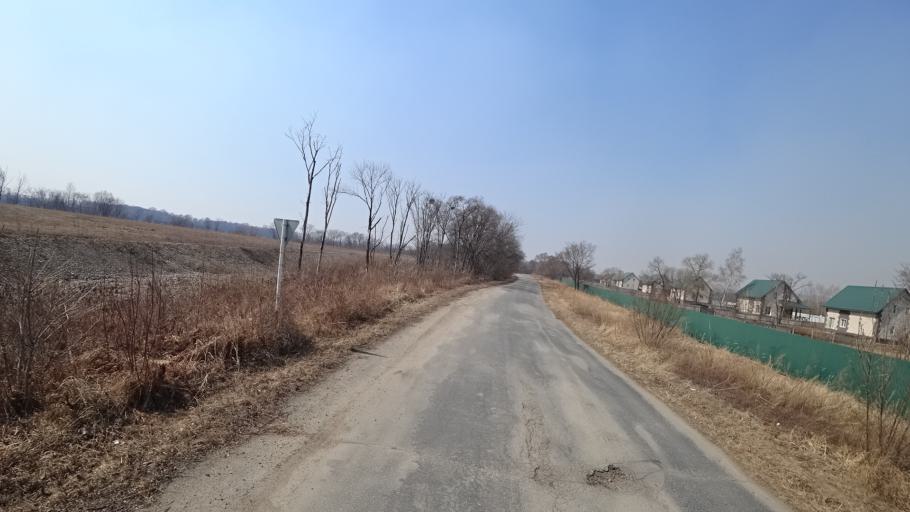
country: RU
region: Amur
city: Novobureyskiy
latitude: 49.7853
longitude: 129.9192
